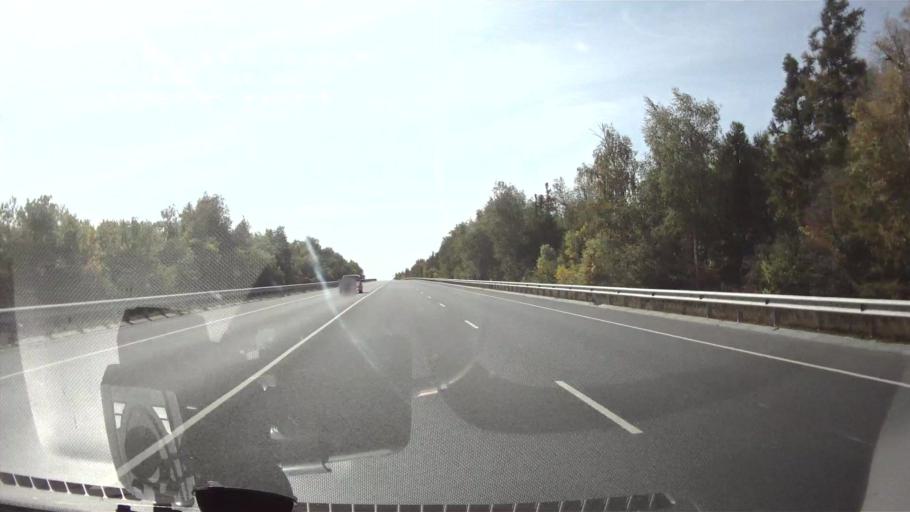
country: RU
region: Saratov
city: Khvalynsk
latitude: 52.5645
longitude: 48.0934
